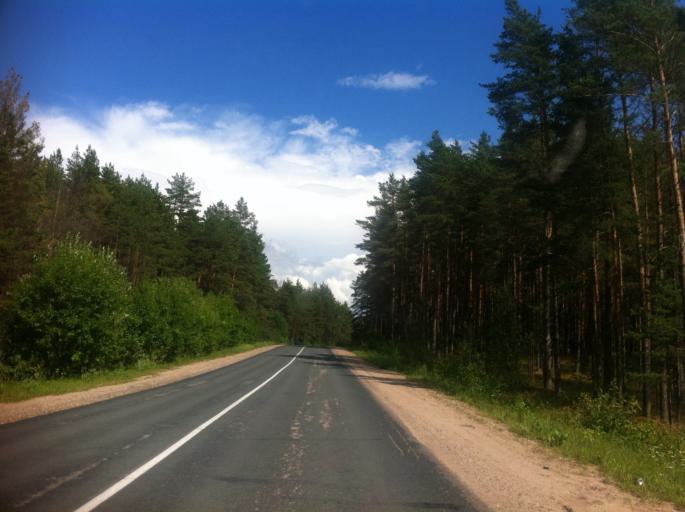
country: RU
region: Pskov
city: Izborsk
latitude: 57.8346
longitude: 27.9404
